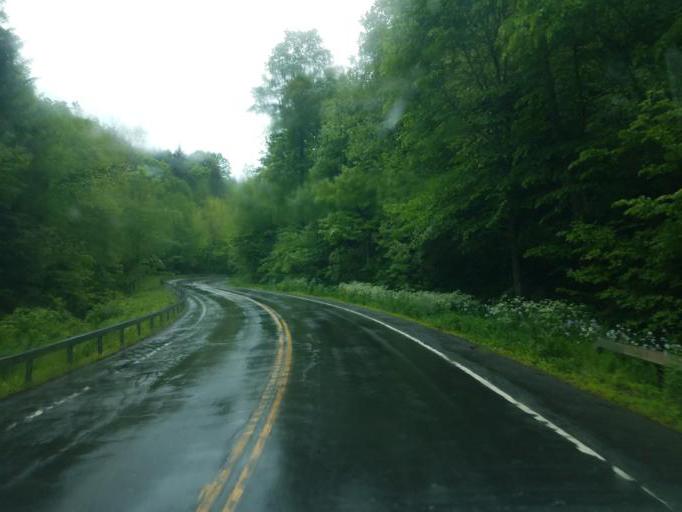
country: US
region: New York
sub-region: Herkimer County
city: Frankfort
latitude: 42.9578
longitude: -75.1112
